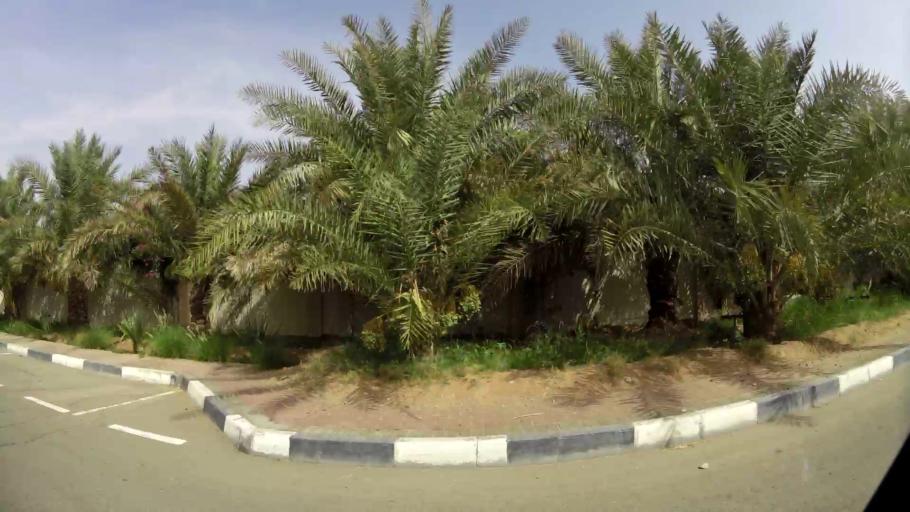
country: AE
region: Abu Dhabi
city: Al Ain
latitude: 24.1490
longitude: 55.6884
